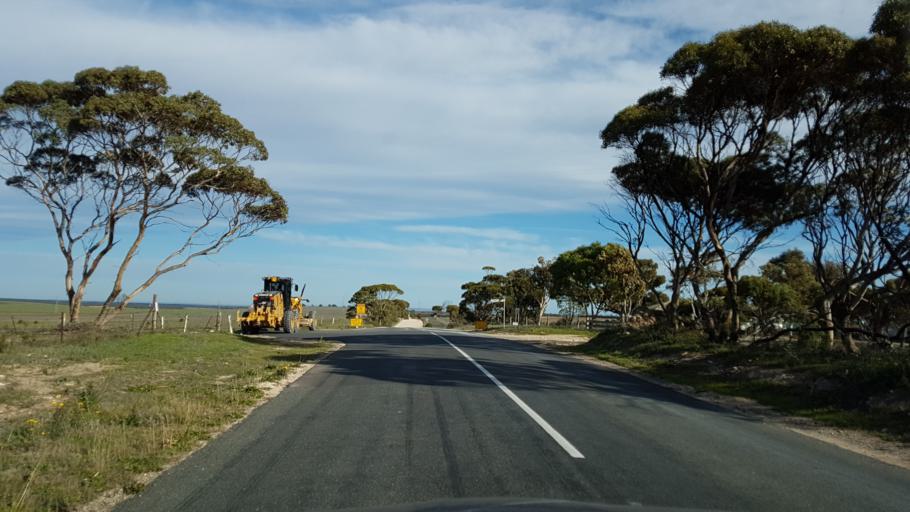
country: AU
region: South Australia
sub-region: Murray Bridge
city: Tailem Bend
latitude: -35.1832
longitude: 139.4557
